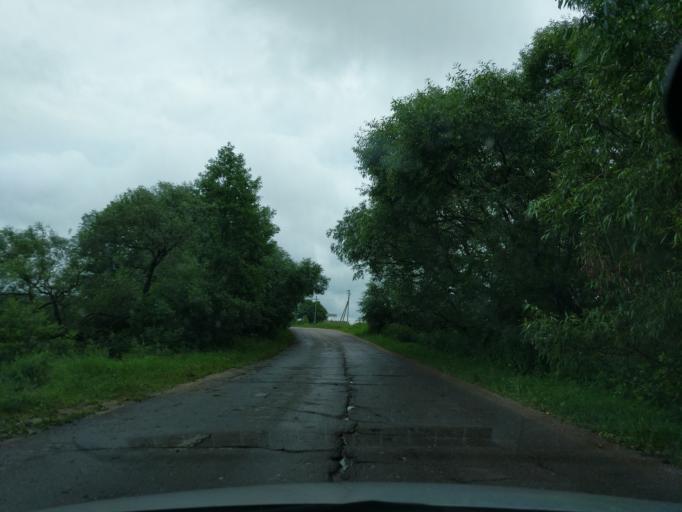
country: RU
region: Kaluga
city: Myatlevo
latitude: 54.8342
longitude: 35.6395
